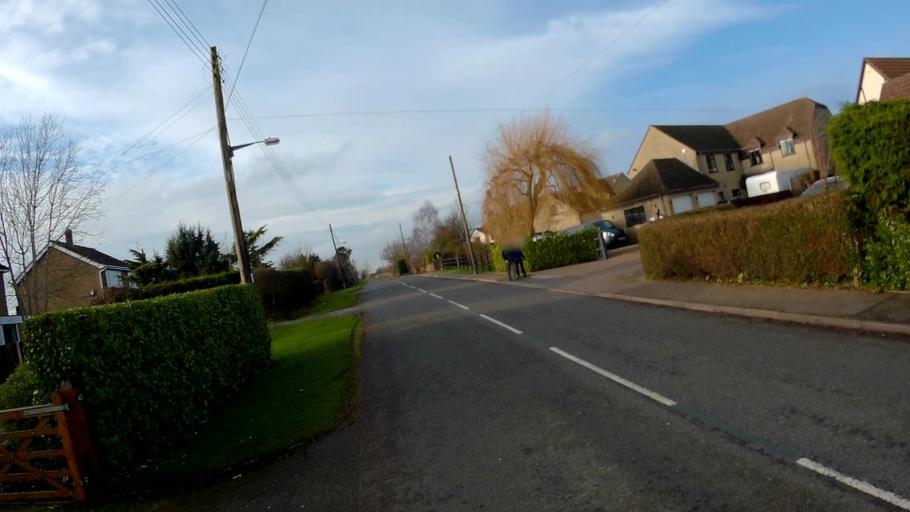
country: GB
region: England
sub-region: Lincolnshire
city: Bourne
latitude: 52.7370
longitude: -0.3919
